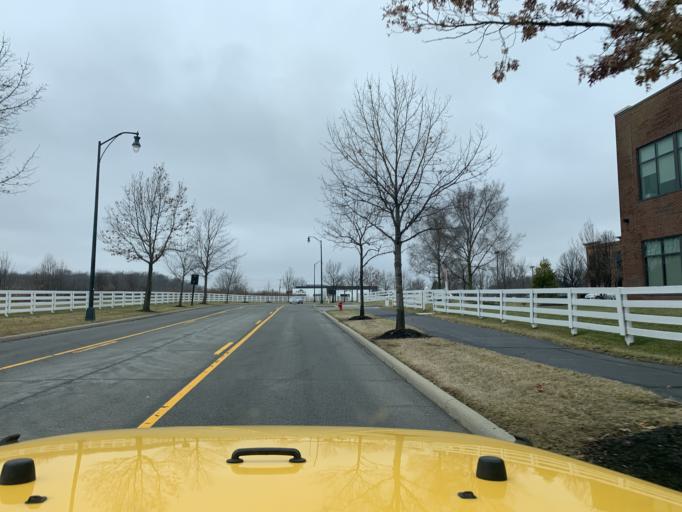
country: US
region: Ohio
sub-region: Franklin County
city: New Albany
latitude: 40.0915
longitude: -82.8076
